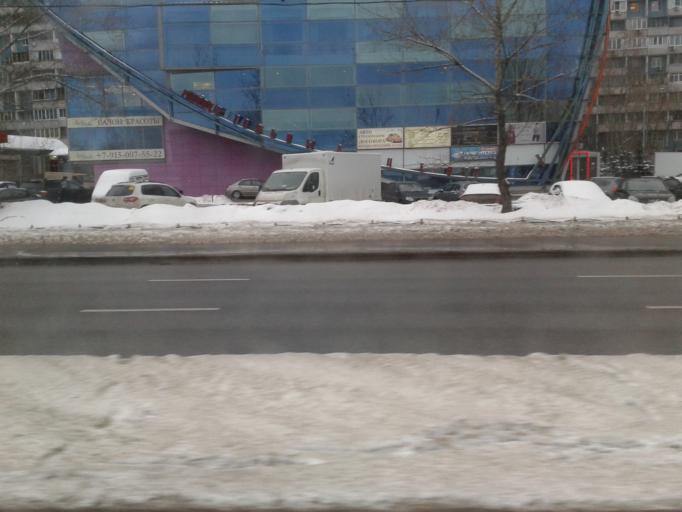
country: RU
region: Moscow
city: Strogino
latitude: 55.8045
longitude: 37.4191
